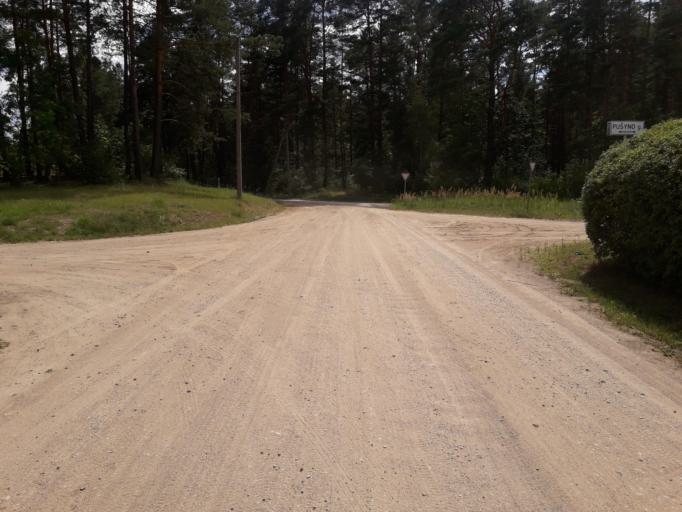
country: LT
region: Alytaus apskritis
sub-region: Alytaus rajonas
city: Daugai
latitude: 54.1647
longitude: 24.1875
